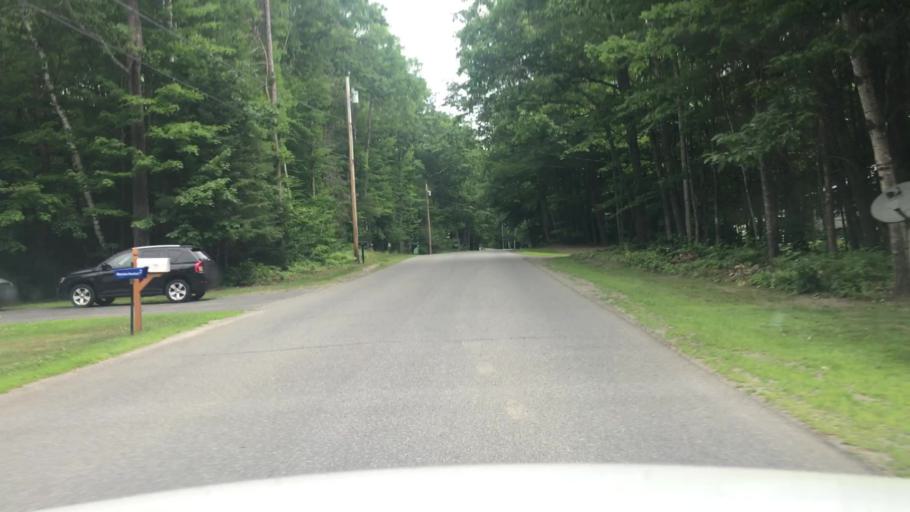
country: US
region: Maine
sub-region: Kennebec County
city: Clinton
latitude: 44.5898
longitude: -69.4708
